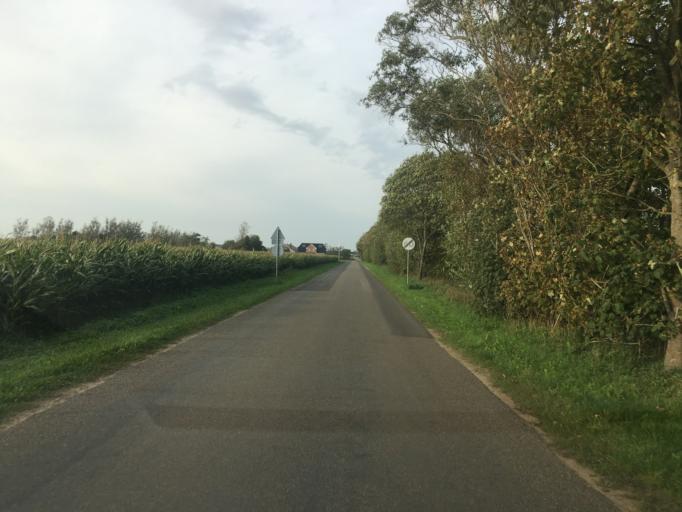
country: DE
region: Schleswig-Holstein
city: Ellhoft
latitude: 54.9231
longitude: 8.9845
